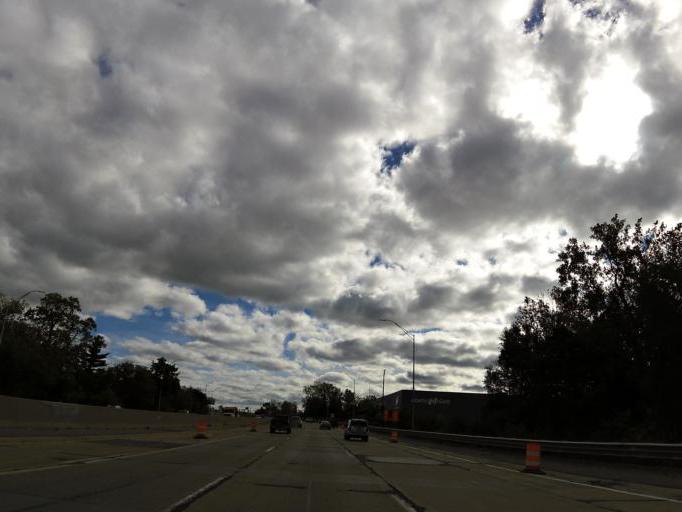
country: US
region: Michigan
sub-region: Genesee County
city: Flint
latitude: 43.0105
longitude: -83.6697
